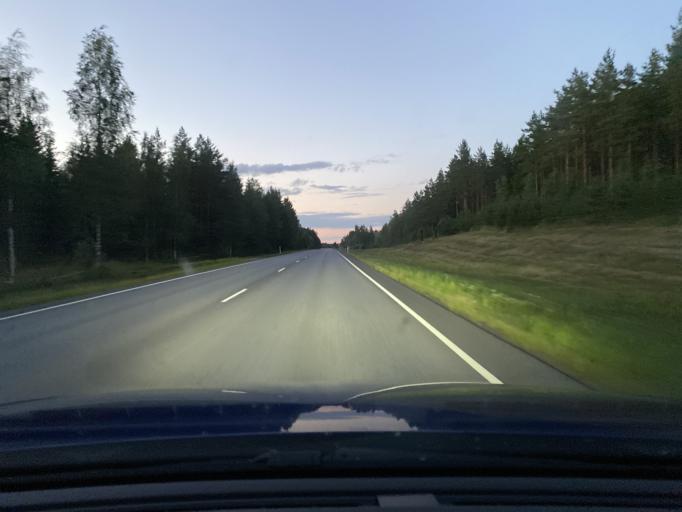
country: FI
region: Varsinais-Suomi
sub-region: Loimaa
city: Oripaeae
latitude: 60.8366
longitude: 22.6647
